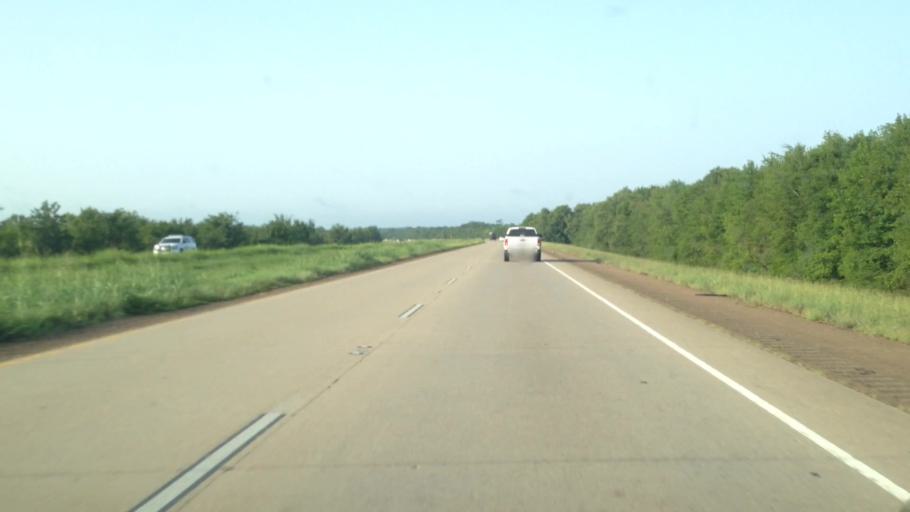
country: US
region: Louisiana
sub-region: Rapides Parish
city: Woodworth
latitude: 31.2087
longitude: -92.4722
